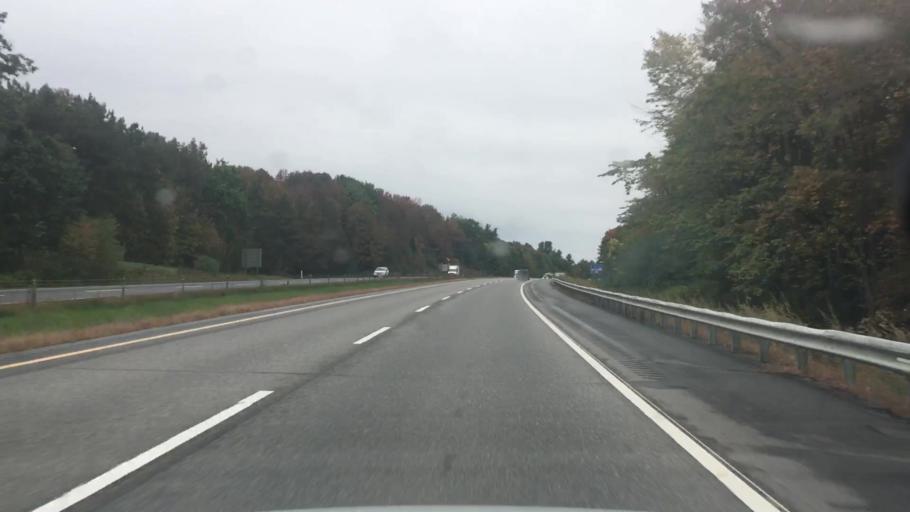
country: US
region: Maine
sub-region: Kennebec County
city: Augusta
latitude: 44.3268
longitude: -69.8149
